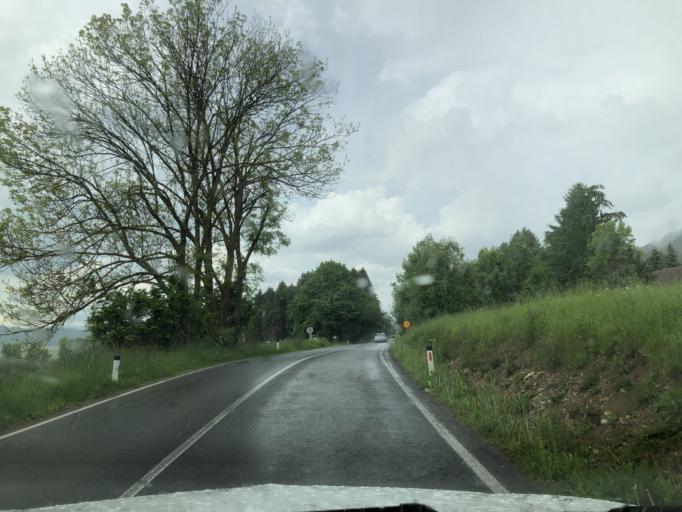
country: SI
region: Cerknica
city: Cerknica
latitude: 45.7796
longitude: 14.3919
